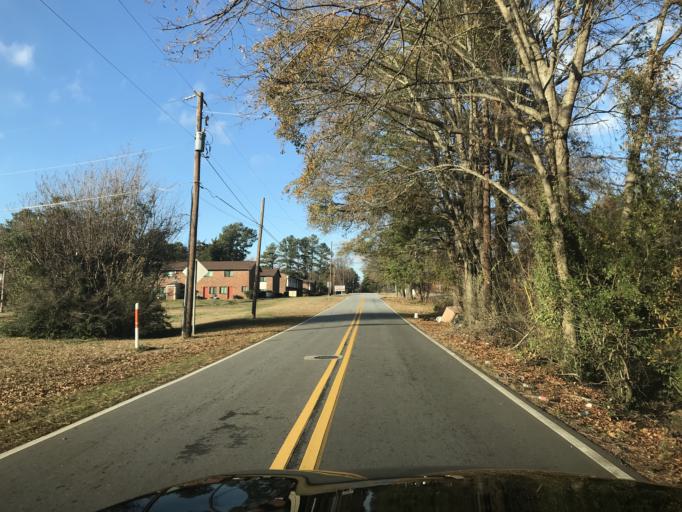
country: US
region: Georgia
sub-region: Fulton County
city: College Park
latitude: 33.6251
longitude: -84.4875
